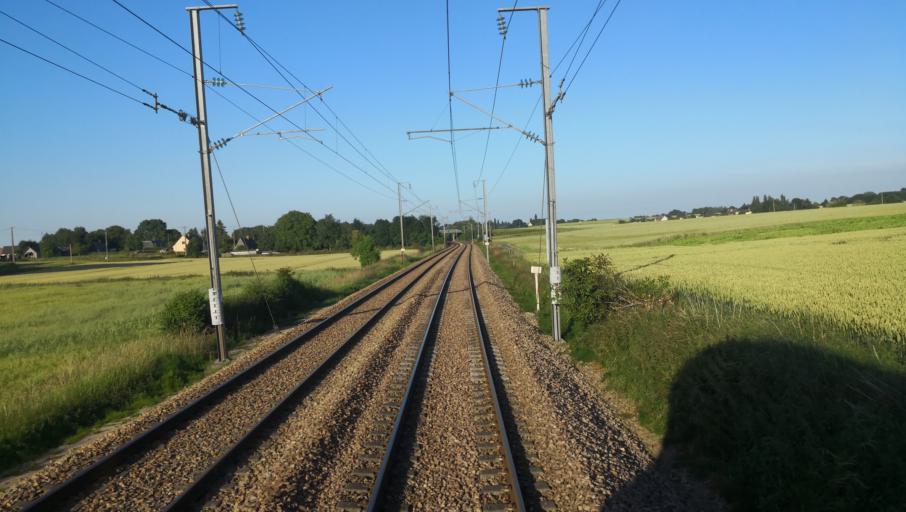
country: FR
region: Haute-Normandie
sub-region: Departement de l'Eure
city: Thiberville
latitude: 49.0808
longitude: 0.4960
